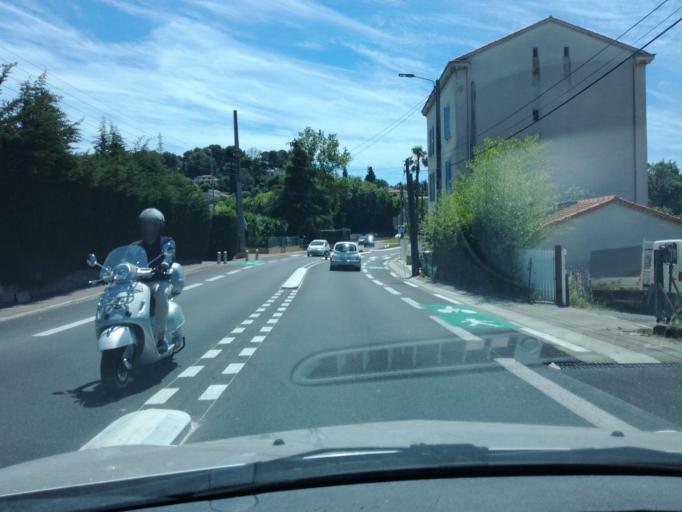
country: FR
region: Provence-Alpes-Cote d'Azur
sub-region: Departement des Alpes-Maritimes
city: Mougins
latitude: 43.5909
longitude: 7.0029
